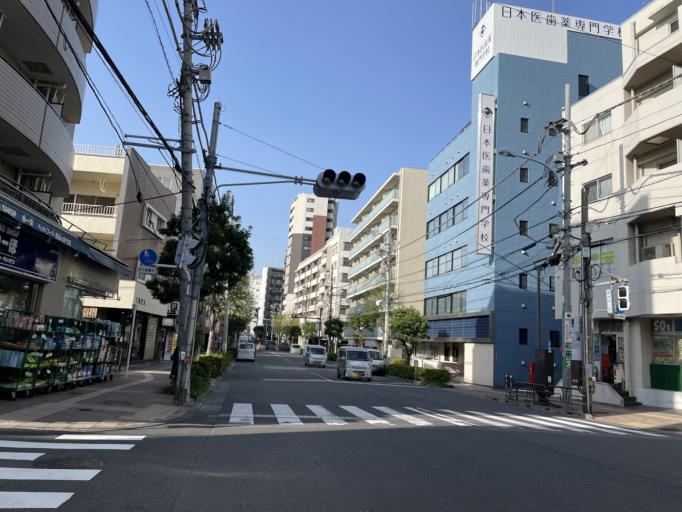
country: JP
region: Tokyo
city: Tokyo
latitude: 35.7010
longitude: 139.6495
